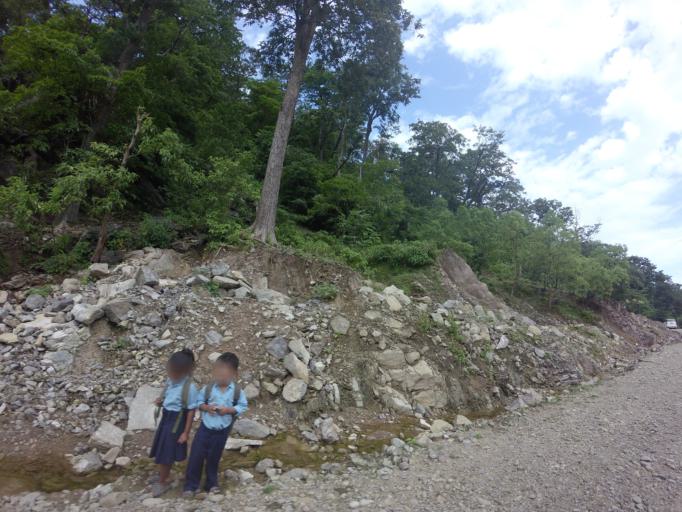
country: NP
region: Far Western
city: Tikapur
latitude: 28.6530
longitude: 81.2870
